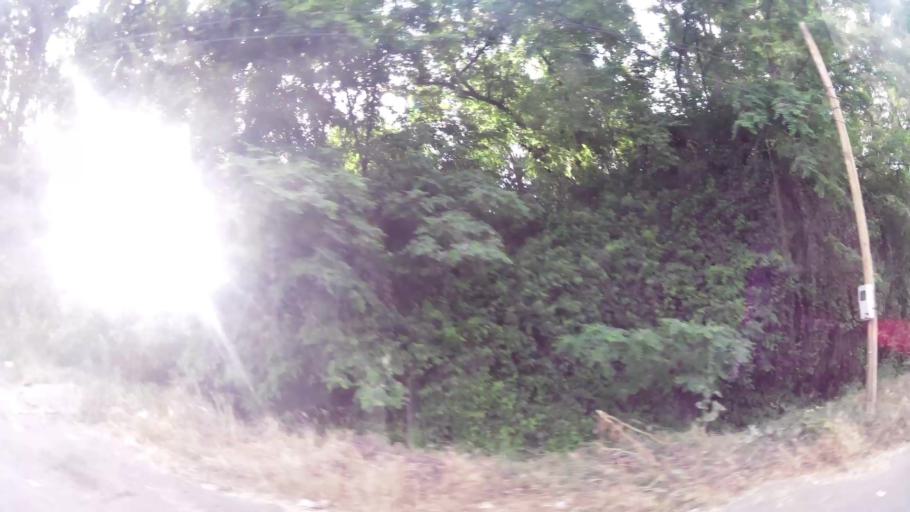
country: CL
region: Santiago Metropolitan
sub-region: Provincia de Maipo
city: San Bernardo
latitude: -33.6441
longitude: -70.6651
